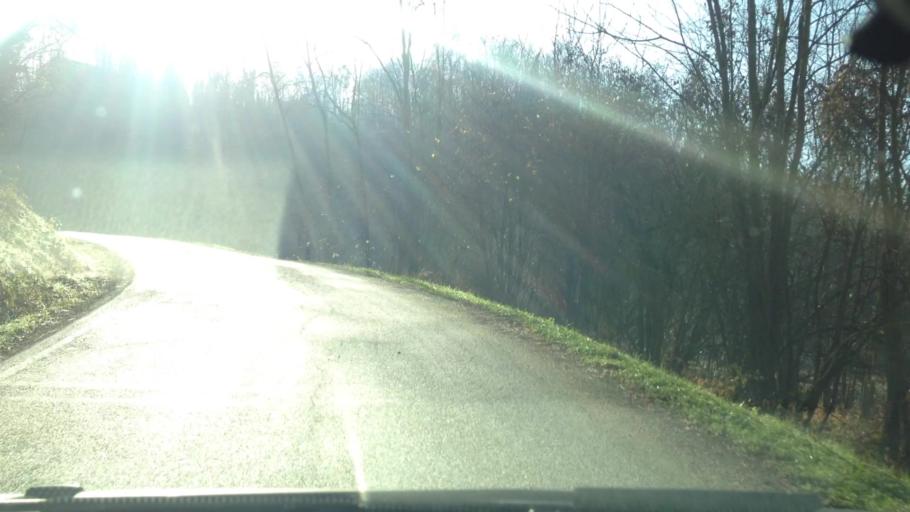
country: IT
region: Piedmont
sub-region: Provincia di Alessandria
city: Masio
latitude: 44.8553
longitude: 8.4149
